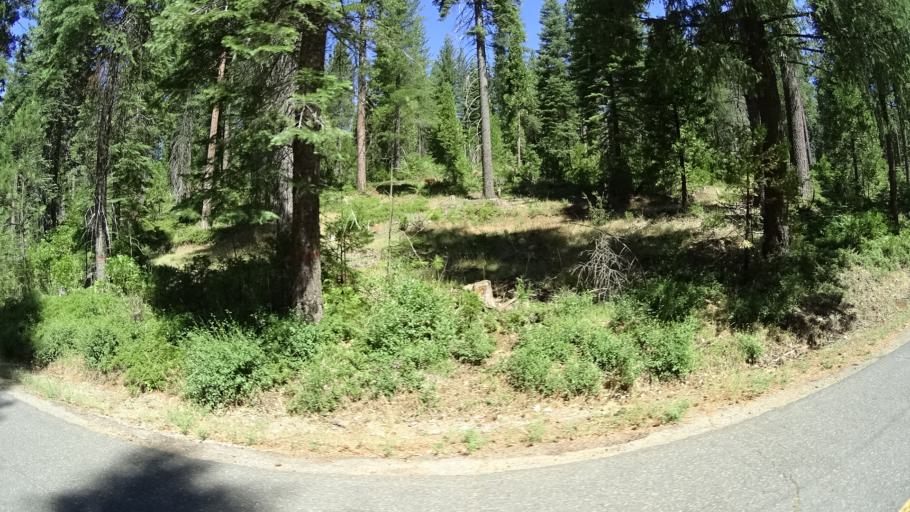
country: US
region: California
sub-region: Amador County
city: Pioneer
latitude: 38.4369
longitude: -120.4349
